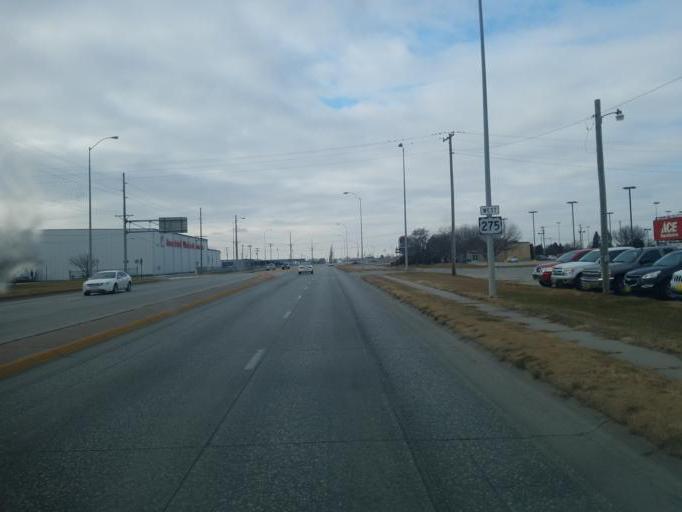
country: US
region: Nebraska
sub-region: Madison County
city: Norfolk
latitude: 42.0182
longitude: -97.4276
